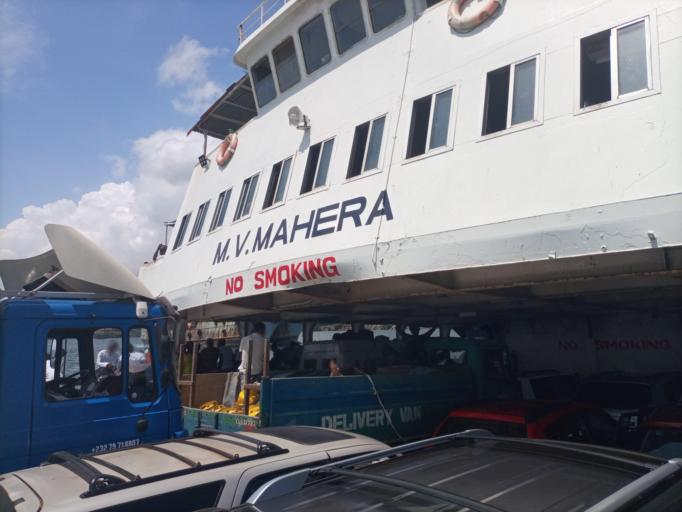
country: SL
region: Western Area
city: Freetown
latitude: 8.4899
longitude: -13.1931
